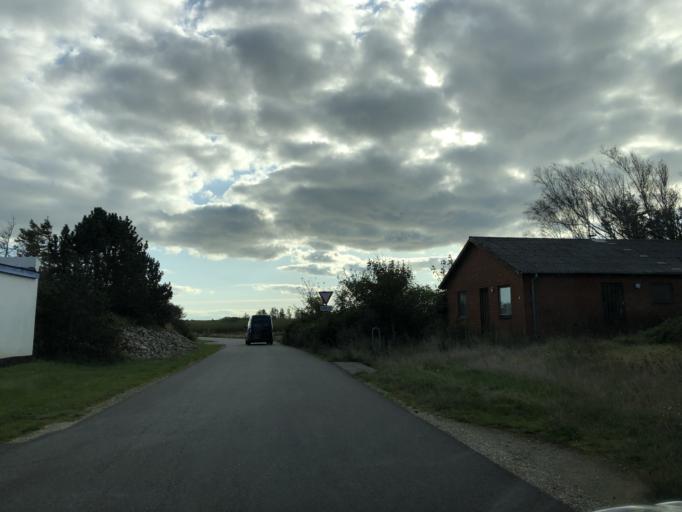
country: DK
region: Central Jutland
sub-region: Holstebro Kommune
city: Ulfborg
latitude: 56.3201
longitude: 8.1577
